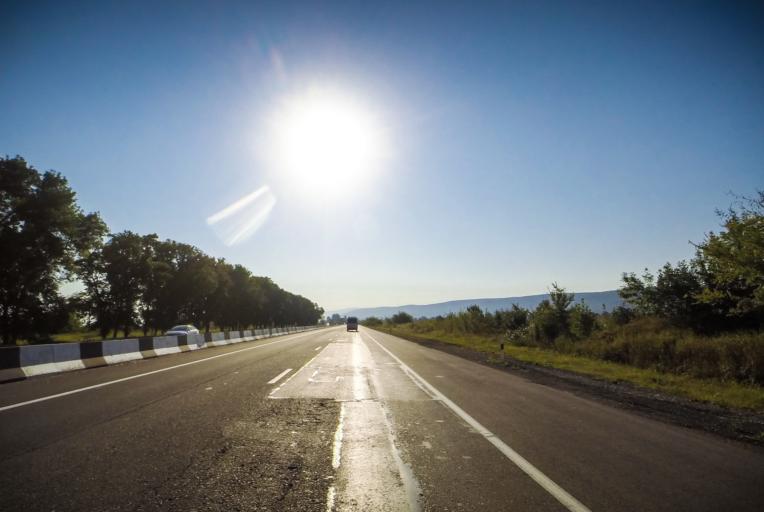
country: RU
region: North Ossetia
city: Zmeyskaya
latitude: 43.3226
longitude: 44.1070
